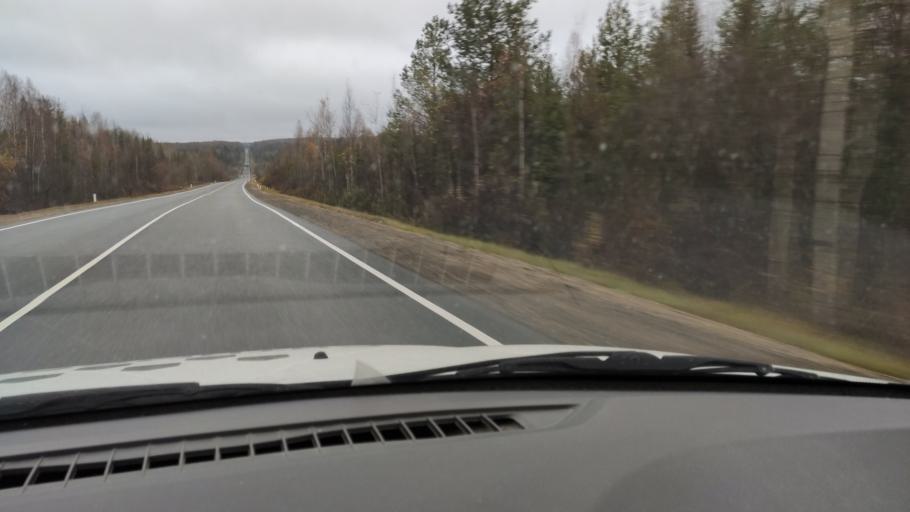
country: RU
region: Kirov
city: Omutninsk
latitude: 58.7208
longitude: 52.0861
